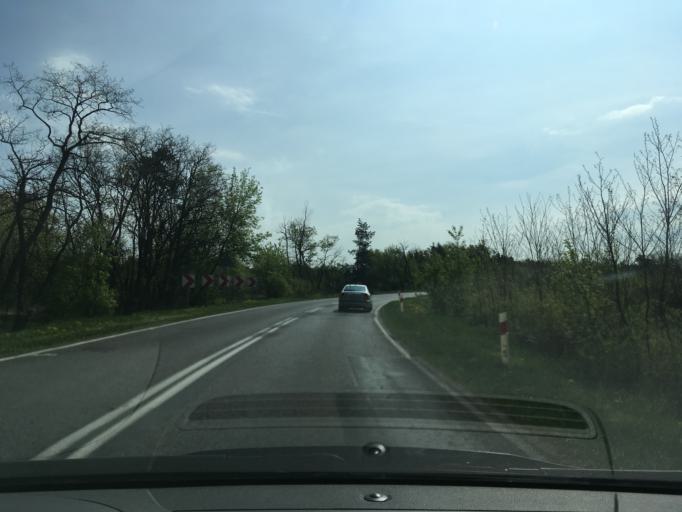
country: PL
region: Lublin Voivodeship
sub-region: Powiat pulawski
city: Pulawy
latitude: 51.4613
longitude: 21.9435
